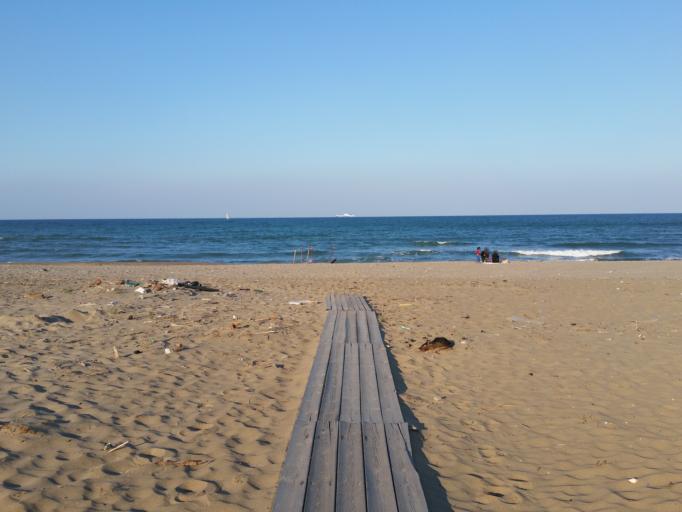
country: IT
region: Sicily
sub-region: Catania
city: Catania
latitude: 37.4476
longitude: 15.0864
